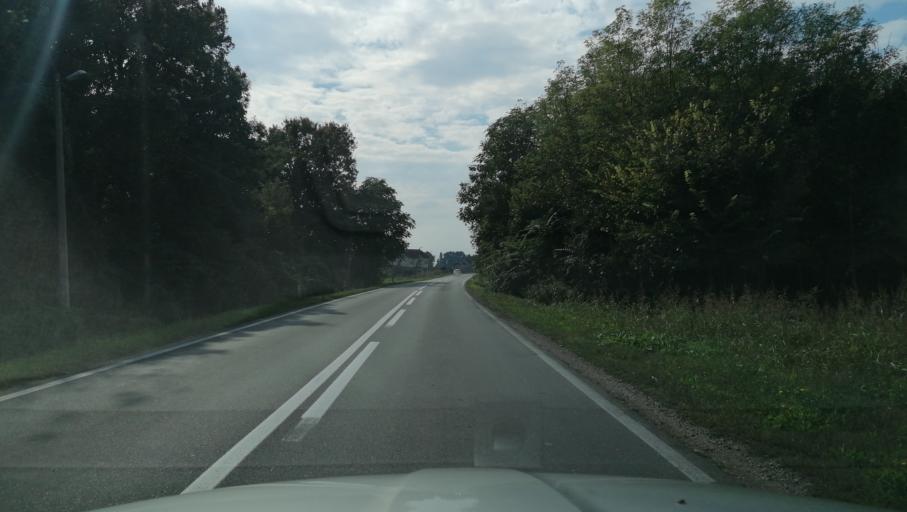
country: BA
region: Republika Srpska
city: Dvorovi
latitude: 44.8307
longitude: 19.2922
